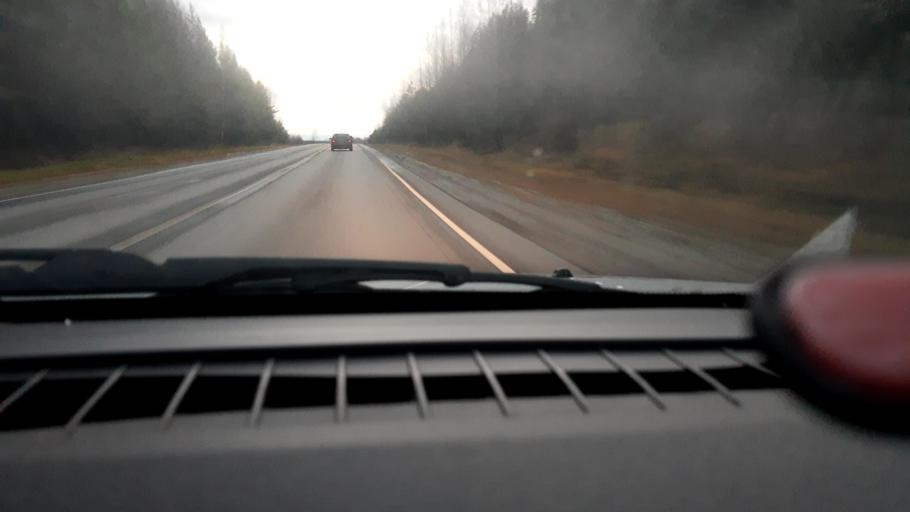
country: RU
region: Nizjnij Novgorod
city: Vladimirskoye
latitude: 56.9678
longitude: 45.1101
